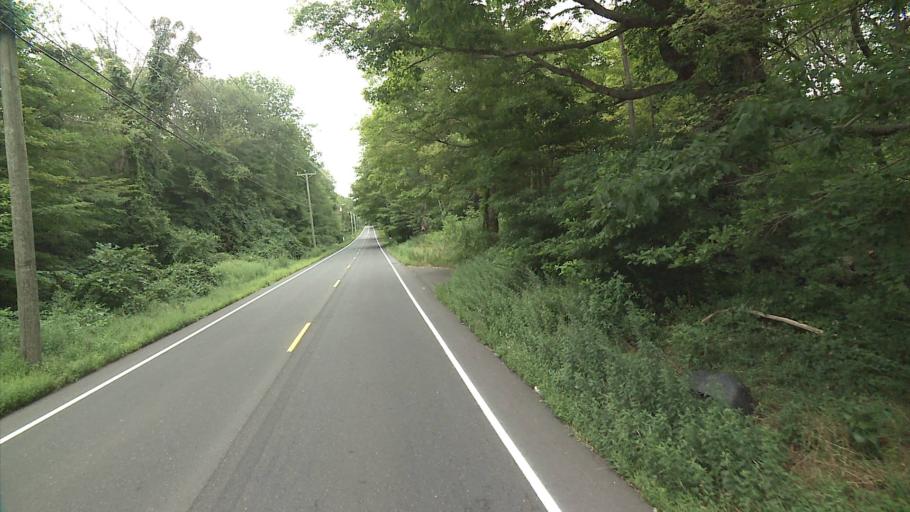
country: US
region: Connecticut
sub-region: New London County
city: Colchester
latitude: 41.5368
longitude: -72.3012
